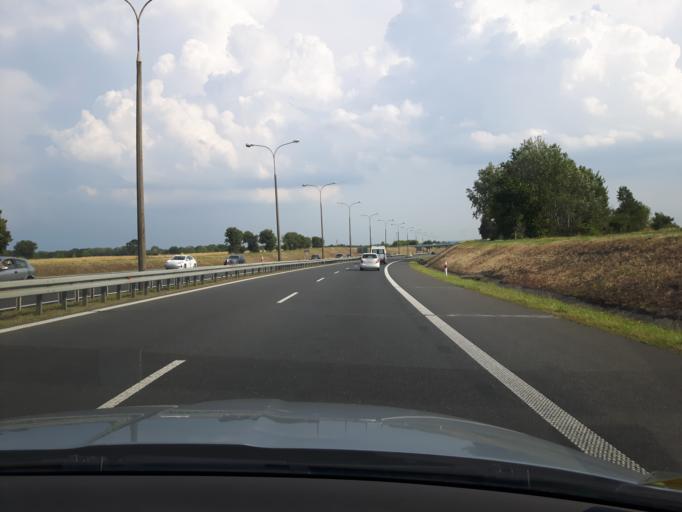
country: PL
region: Masovian Voivodeship
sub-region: Powiat nowodworski
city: Zakroczym
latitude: 52.4384
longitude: 20.6461
